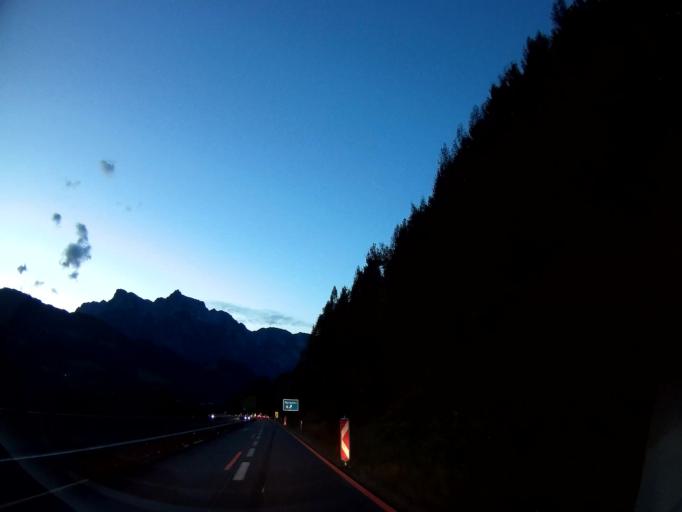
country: AT
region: Salzburg
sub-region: Politischer Bezirk Sankt Johann im Pongau
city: Werfen
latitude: 47.4344
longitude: 13.1764
